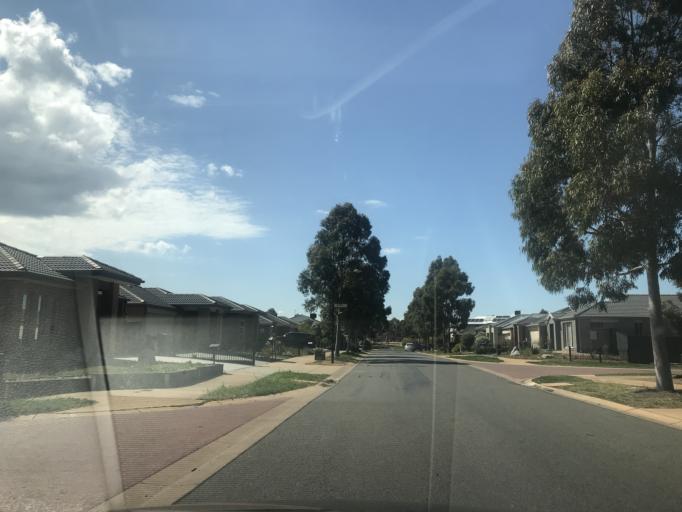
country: AU
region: Victoria
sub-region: Wyndham
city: Hoppers Crossing
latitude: -37.8904
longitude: 144.7222
